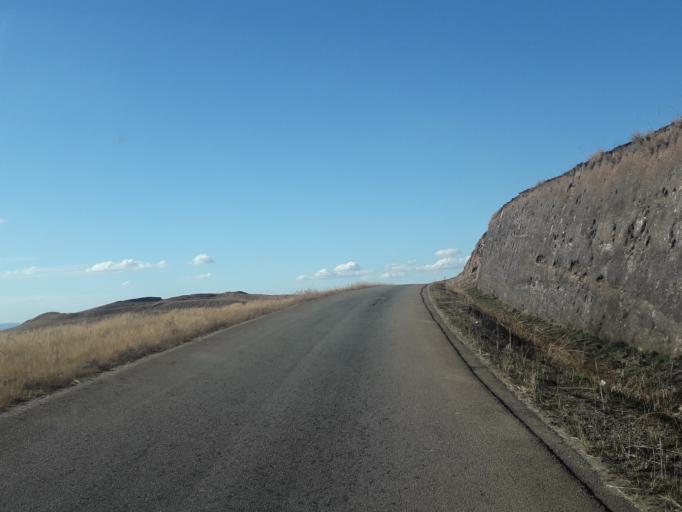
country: MG
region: Analamanga
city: Ankazobe
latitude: -17.8749
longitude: 47.0534
